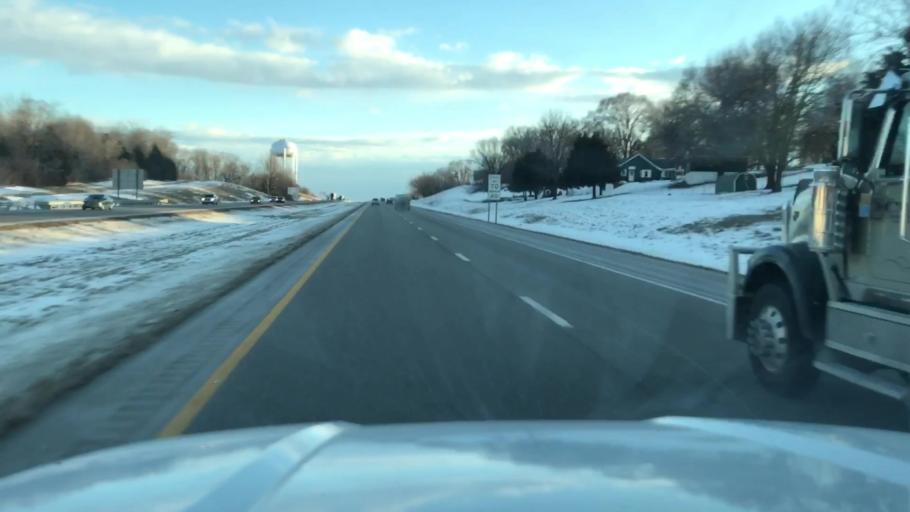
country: US
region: Missouri
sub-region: Andrew County
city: Country Club Village
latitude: 39.8050
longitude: -94.8006
